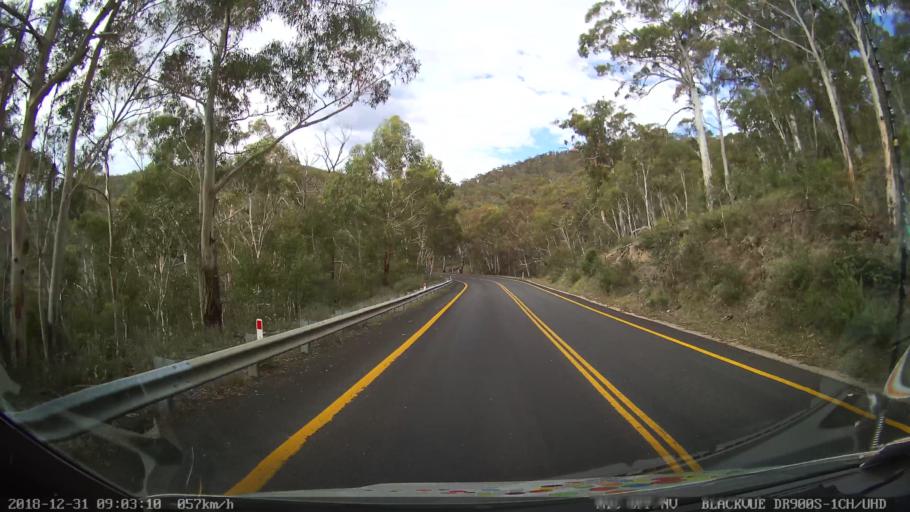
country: AU
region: New South Wales
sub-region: Snowy River
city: Jindabyne
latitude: -36.3458
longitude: 148.5808
